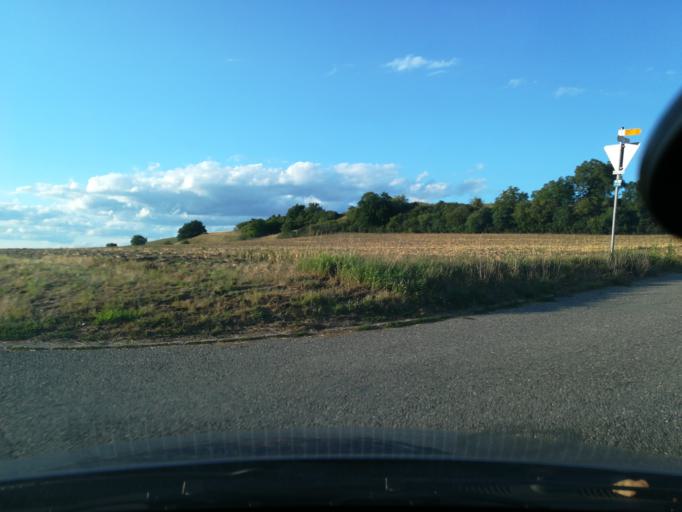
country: DE
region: Baden-Wuerttemberg
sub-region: Freiburg Region
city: Moos
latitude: 47.7277
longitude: 8.8880
